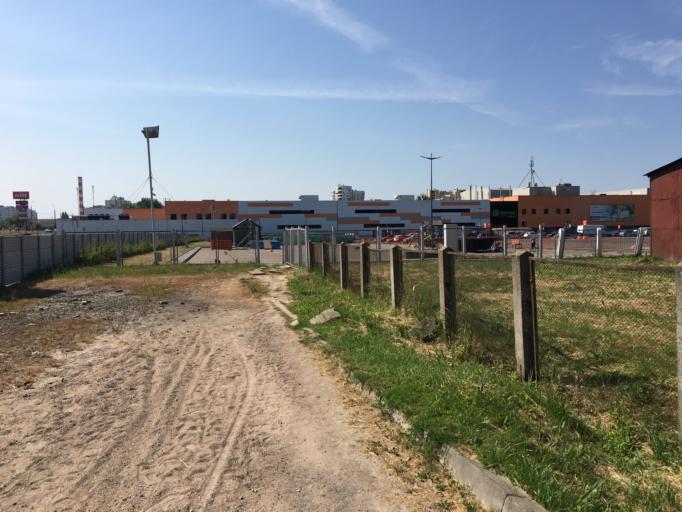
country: BY
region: Grodnenskaya
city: Hrodna
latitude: 53.7035
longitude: 23.8360
